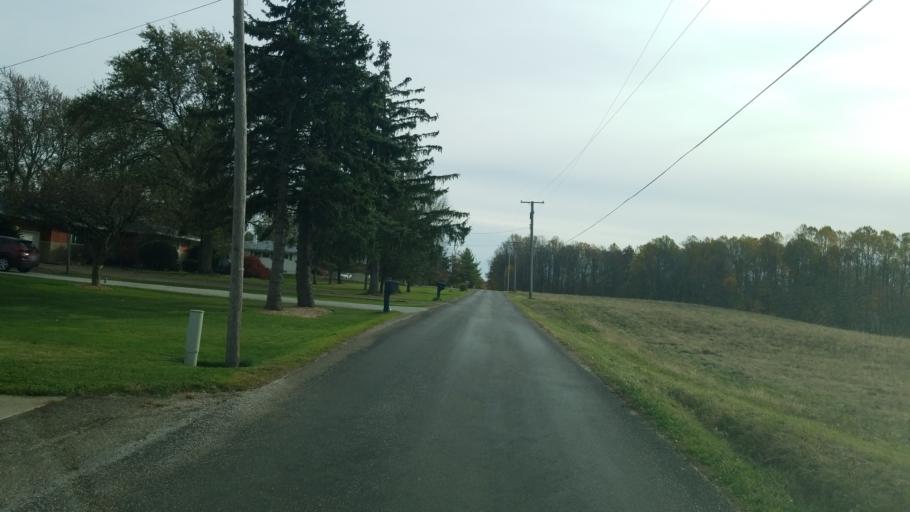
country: US
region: Ohio
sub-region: Richland County
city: Lincoln Heights
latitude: 40.7150
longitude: -82.4552
